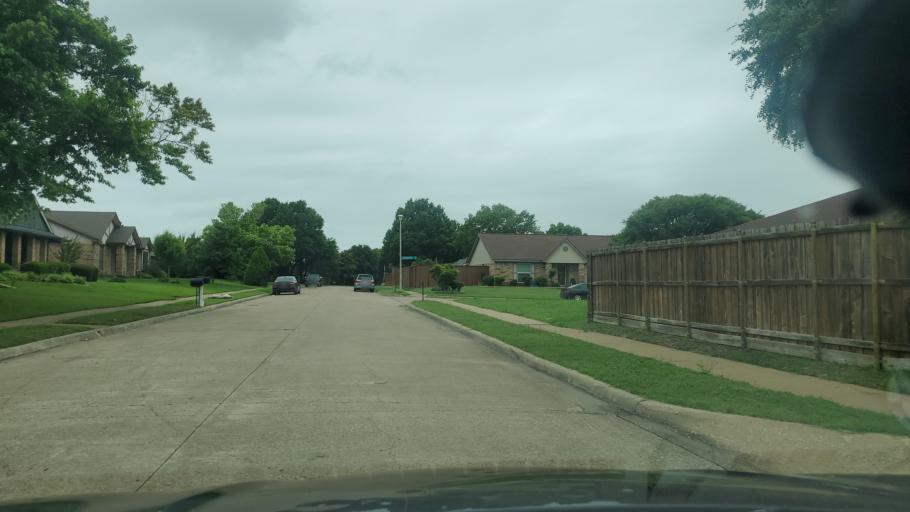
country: US
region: Texas
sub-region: Dallas County
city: Garland
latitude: 32.9388
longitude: -96.6257
